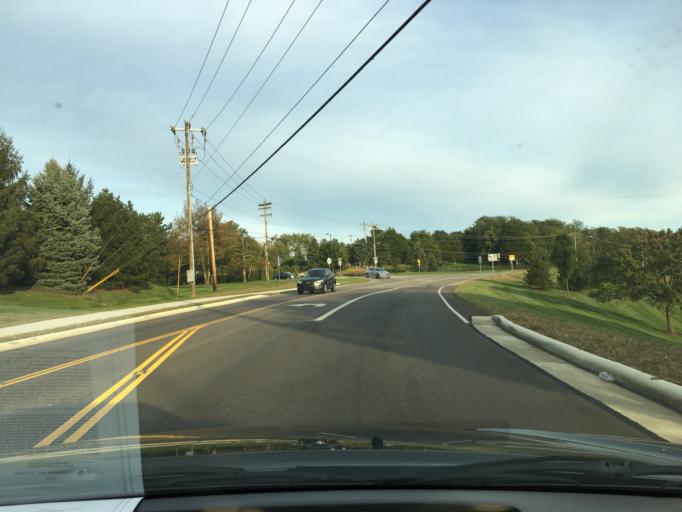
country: US
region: Ohio
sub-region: Butler County
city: Beckett Ridge
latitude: 39.3509
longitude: -84.4523
